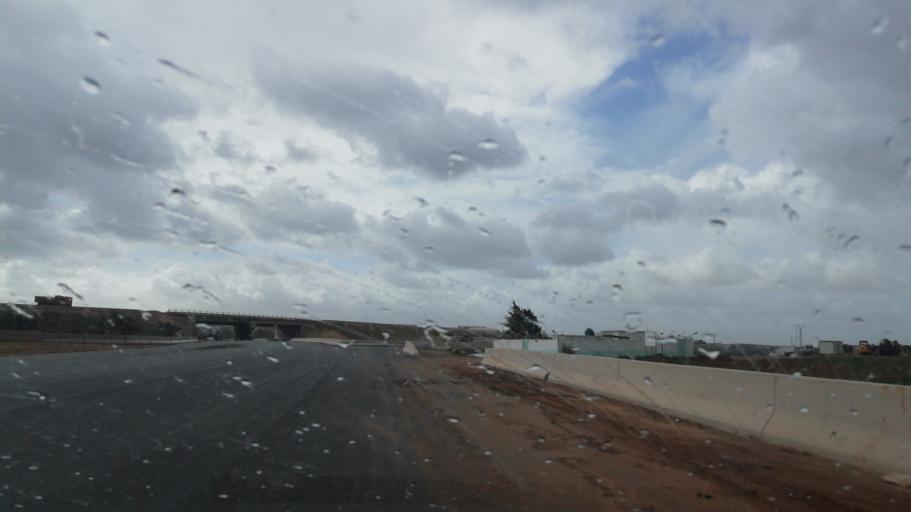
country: DZ
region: Oran
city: Sidi ech Chahmi
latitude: 35.6447
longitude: -0.5254
